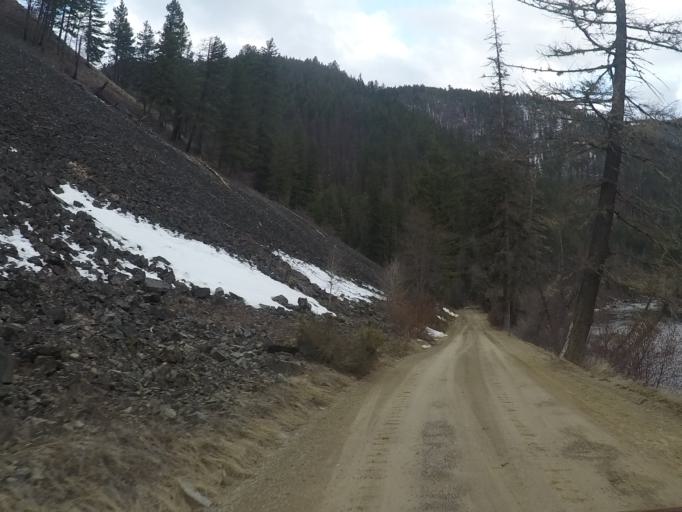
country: US
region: Montana
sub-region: Missoula County
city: Clinton
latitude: 46.5643
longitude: -113.7001
